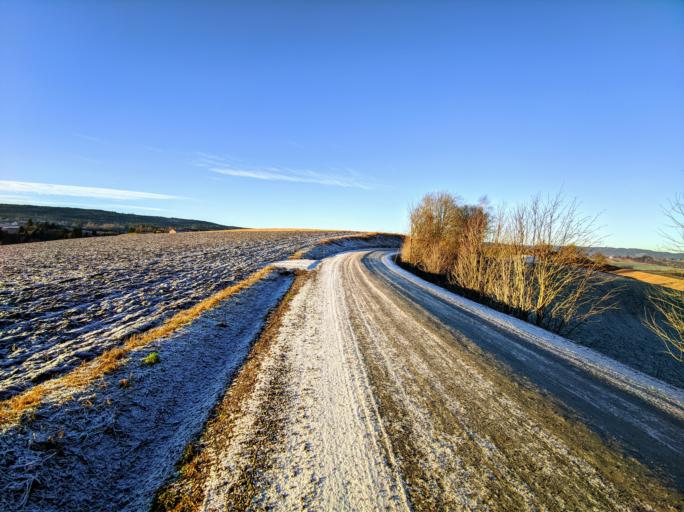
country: NO
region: Akershus
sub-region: Nannestad
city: Teigebyen
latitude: 60.1708
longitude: 11.0187
